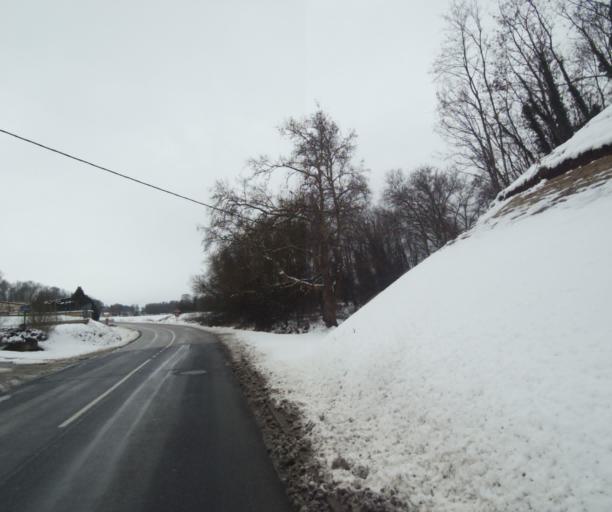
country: FR
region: Champagne-Ardenne
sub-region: Departement de la Haute-Marne
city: Wassy
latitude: 48.4858
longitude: 4.9685
